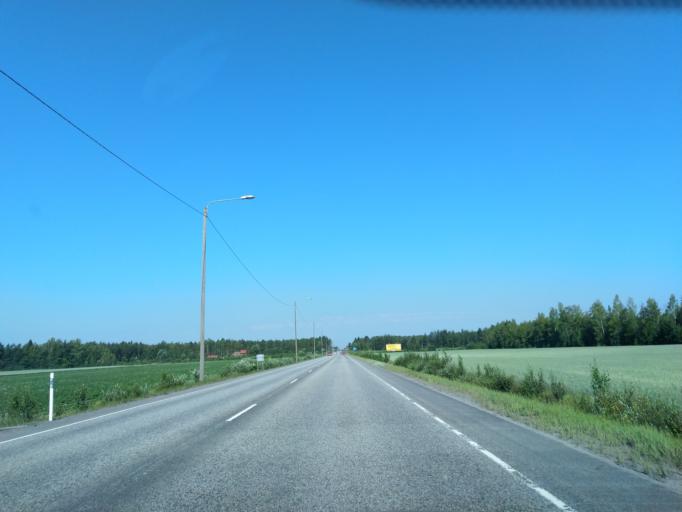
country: FI
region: Satakunta
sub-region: Pori
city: Harjavalta
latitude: 61.3106
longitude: 22.1171
